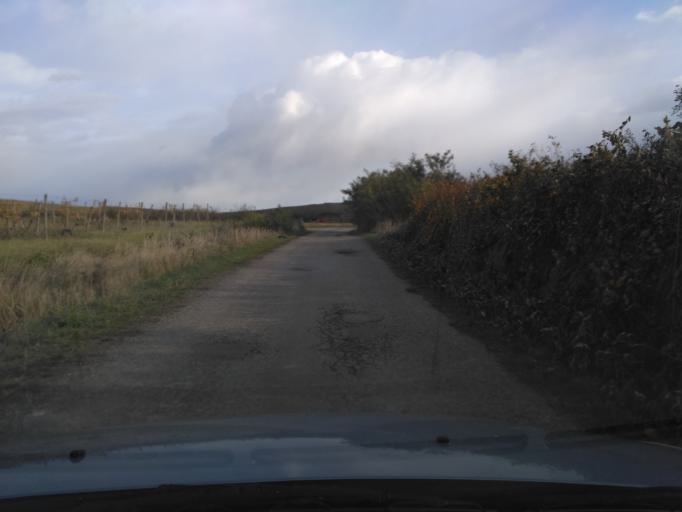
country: HU
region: Borsod-Abauj-Zemplen
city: Satoraljaujhely
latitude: 48.4423
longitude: 21.6971
